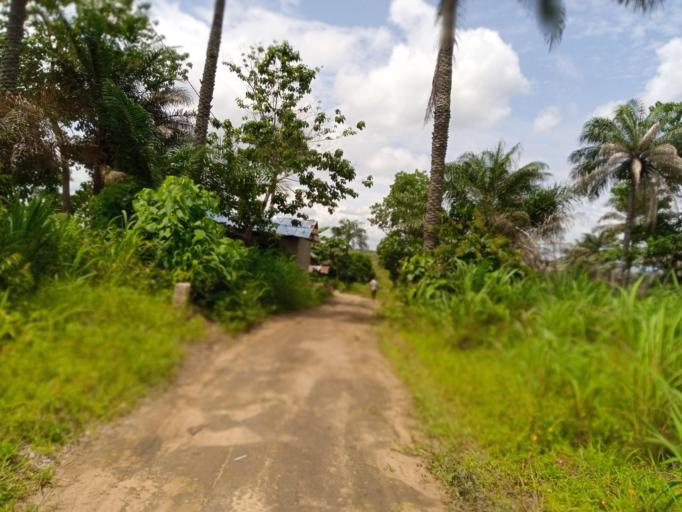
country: SL
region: Northern Province
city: Masoyila
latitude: 8.5455
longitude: -13.1535
